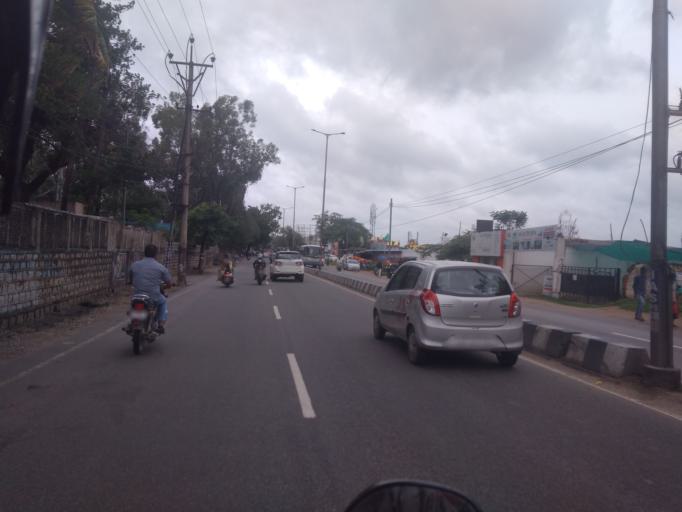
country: IN
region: Telangana
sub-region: Rangareddi
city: Secunderabad
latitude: 17.4968
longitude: 78.5132
